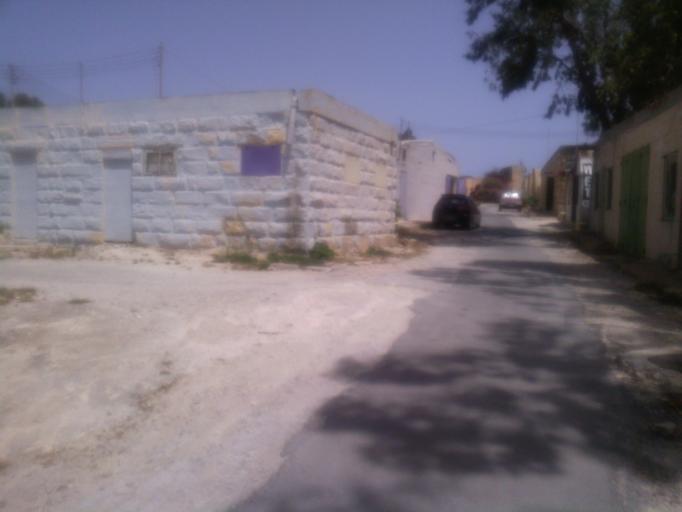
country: MT
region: L-Imdina
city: Imdina
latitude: 35.8906
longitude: 14.4184
